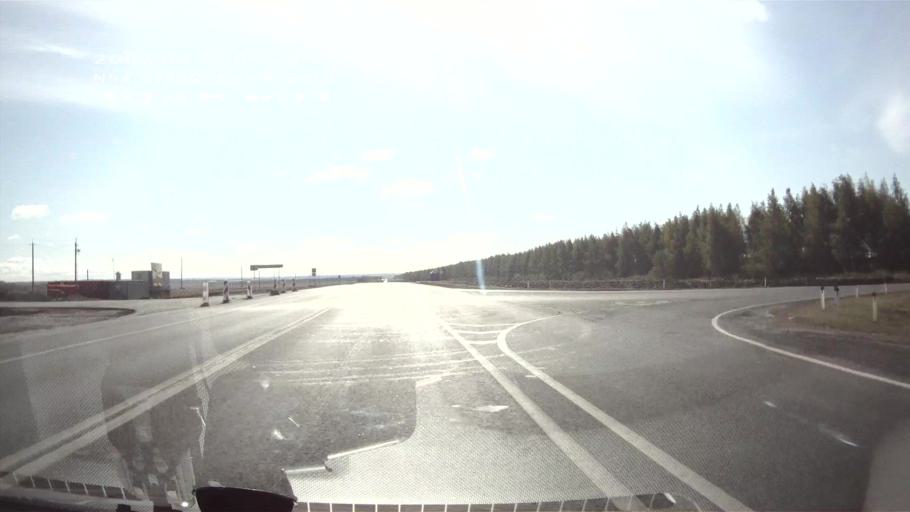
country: RU
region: Ulyanovsk
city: Tsil'na
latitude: 54.5793
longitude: 47.8960
